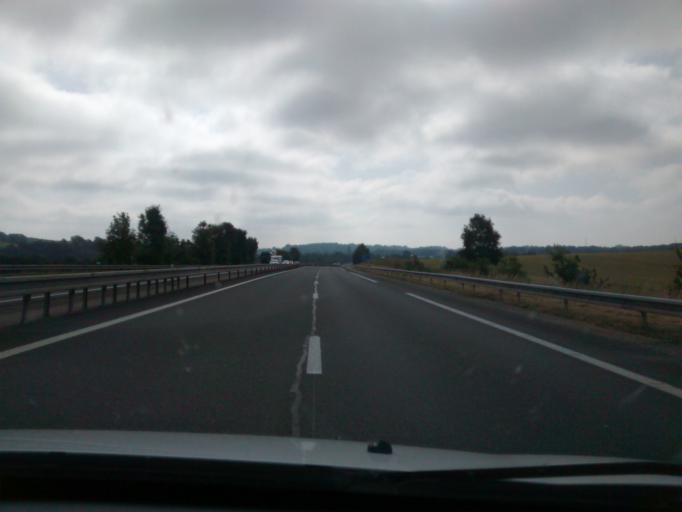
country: FR
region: Pays de la Loire
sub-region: Departement de la Sarthe
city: Trange
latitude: 48.0445
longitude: 0.1192
